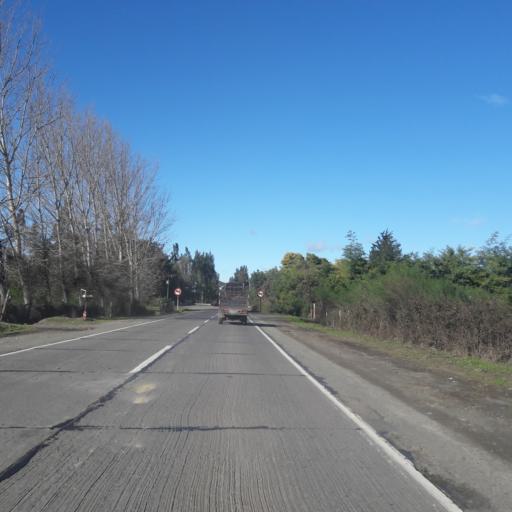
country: CL
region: Araucania
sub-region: Provincia de Malleco
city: Angol
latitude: -37.7399
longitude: -72.6126
